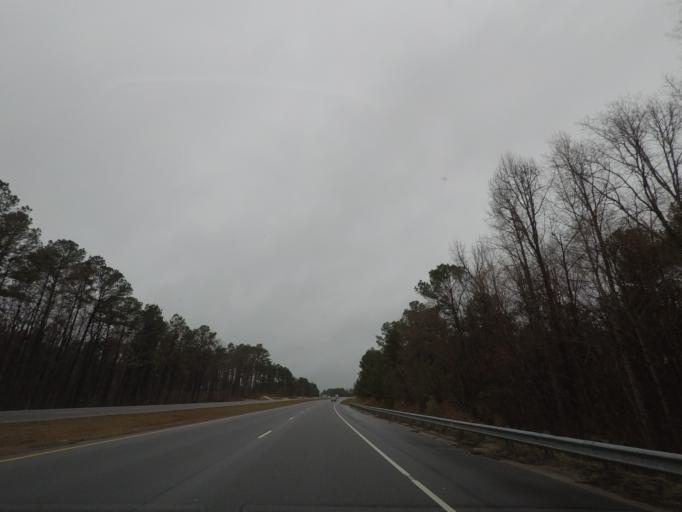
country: US
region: North Carolina
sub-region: Lee County
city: Broadway
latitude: 35.3280
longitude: -79.0936
